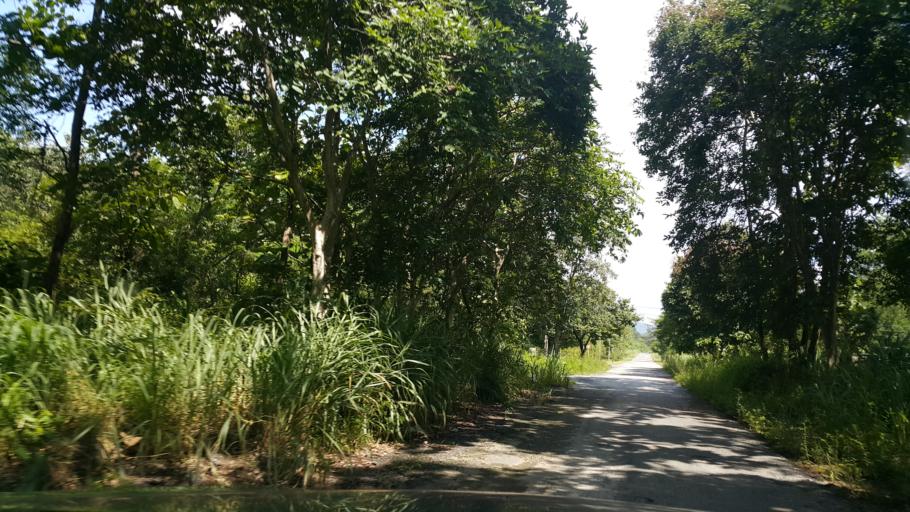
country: TH
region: Chiang Mai
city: San Sai
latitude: 18.9247
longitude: 99.1361
